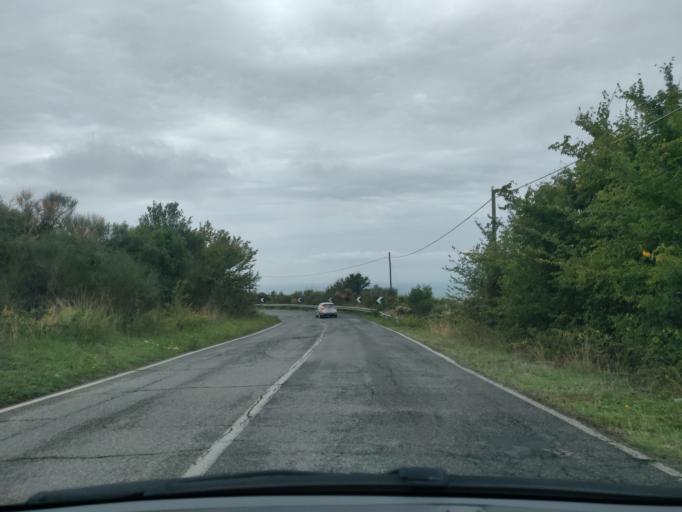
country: IT
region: Latium
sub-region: Citta metropolitana di Roma Capitale
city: Civitavecchia
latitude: 42.1117
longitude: 11.8442
